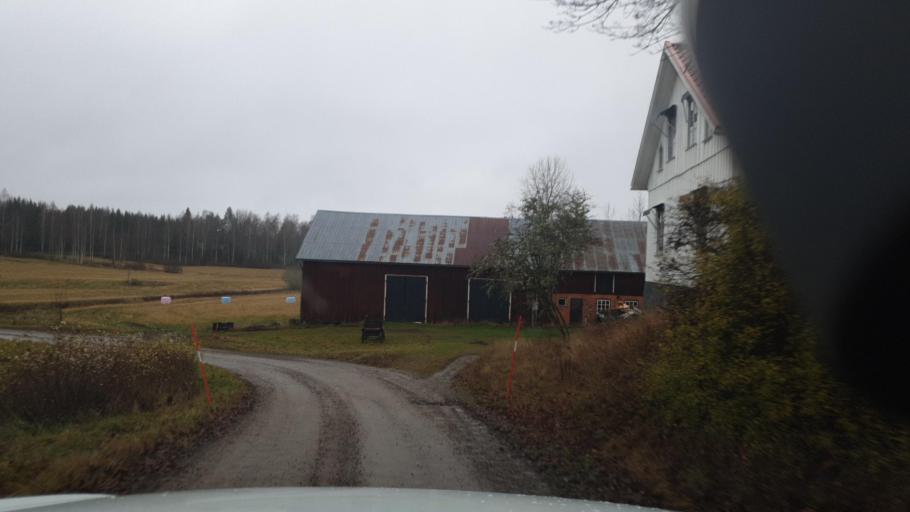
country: SE
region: Vaermland
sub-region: Arvika Kommun
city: Arvika
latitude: 59.5521
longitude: 12.8499
